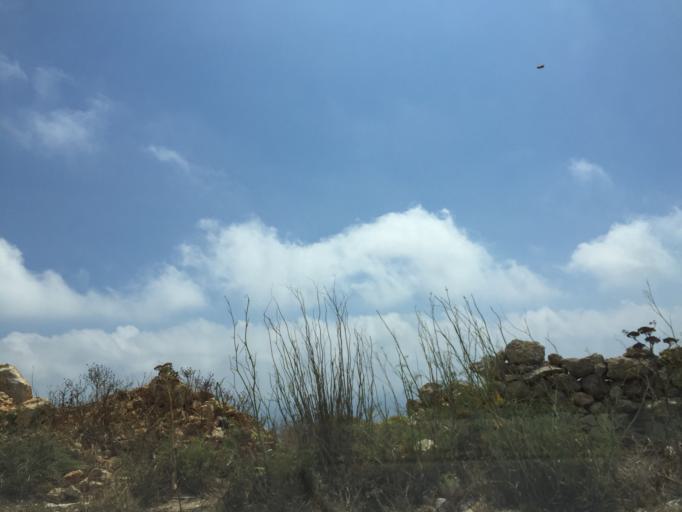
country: MT
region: Dingli
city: Dingli
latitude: 35.8655
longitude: 14.3632
